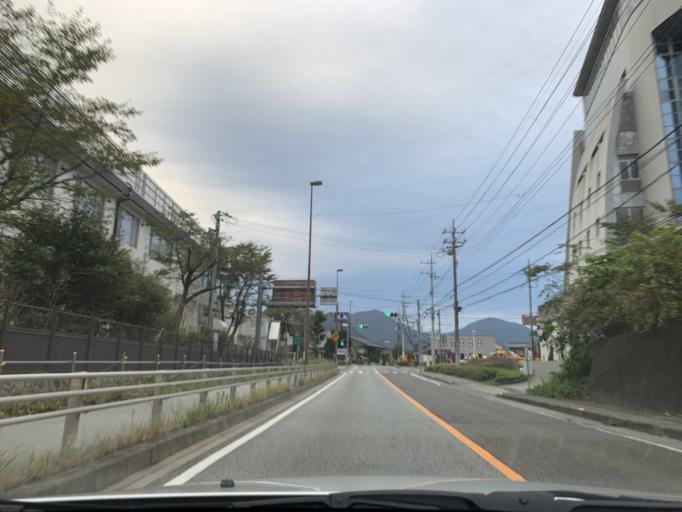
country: JP
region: Yamanashi
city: Otsuki
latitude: 35.6045
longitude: 138.9266
